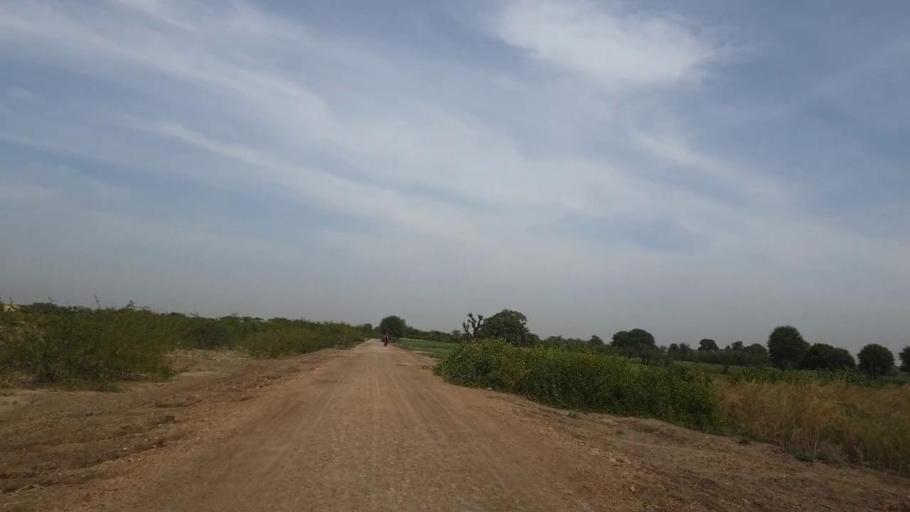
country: PK
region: Sindh
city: Kunri
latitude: 25.1855
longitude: 69.6016
